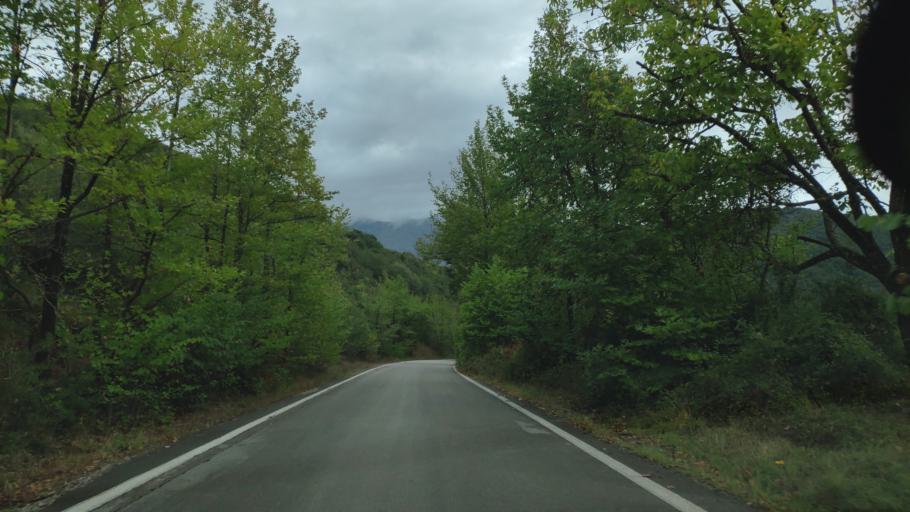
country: GR
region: West Greece
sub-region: Nomos Aitolias kai Akarnanias
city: Sardinia
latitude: 38.9464
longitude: 21.3388
